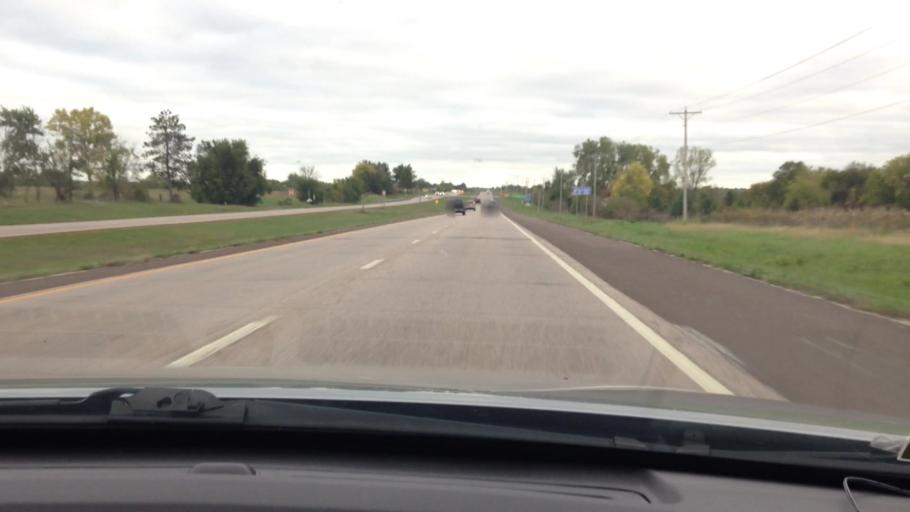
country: US
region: Kansas
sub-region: Leavenworth County
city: Basehor
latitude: 39.1770
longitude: -94.9007
